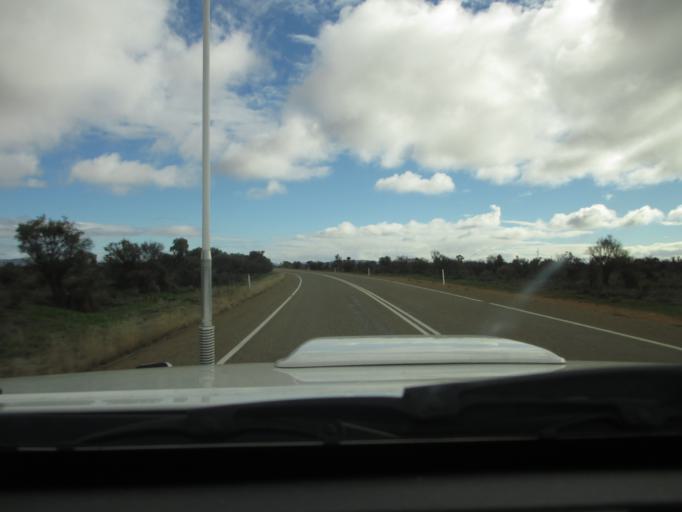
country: AU
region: South Australia
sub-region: Flinders Ranges
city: Quorn
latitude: -32.0767
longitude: 138.5014
